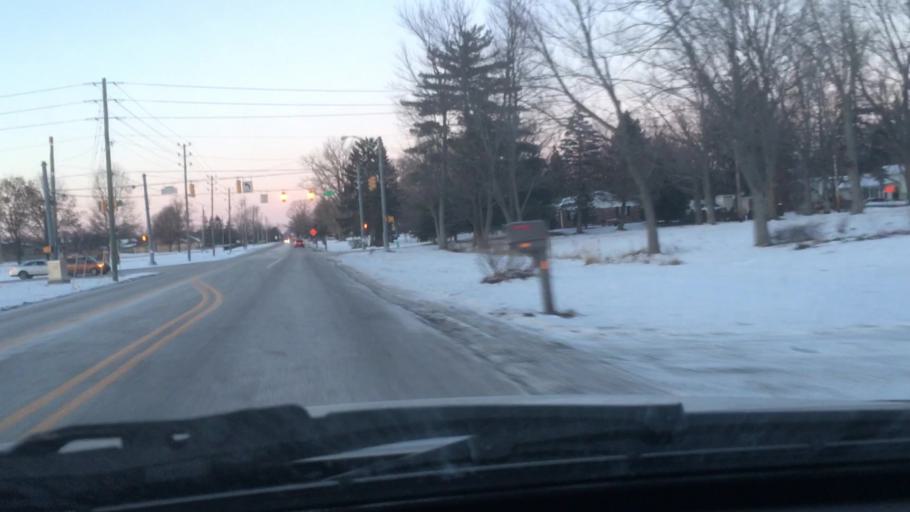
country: US
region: Indiana
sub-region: Marion County
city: Lawrence
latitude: 39.8828
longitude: -86.0330
